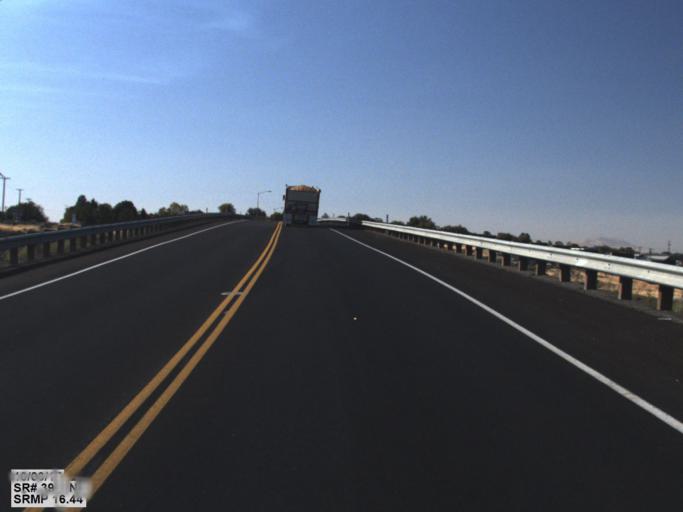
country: US
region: Washington
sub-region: Franklin County
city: Pasco
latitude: 46.1982
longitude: -119.0889
